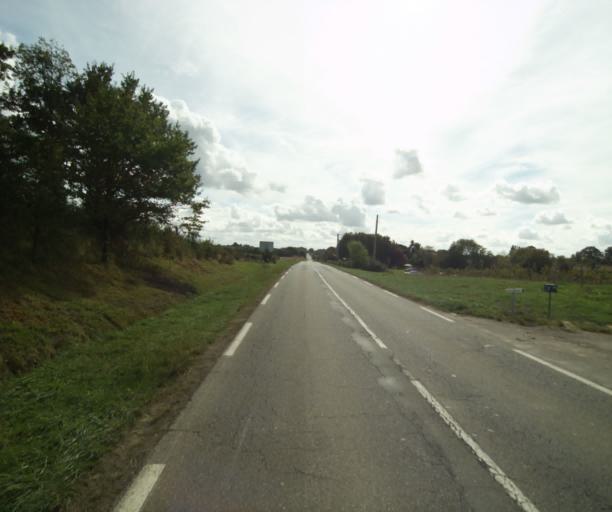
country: FR
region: Midi-Pyrenees
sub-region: Departement du Gers
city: Eauze
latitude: 43.8373
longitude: 0.0926
